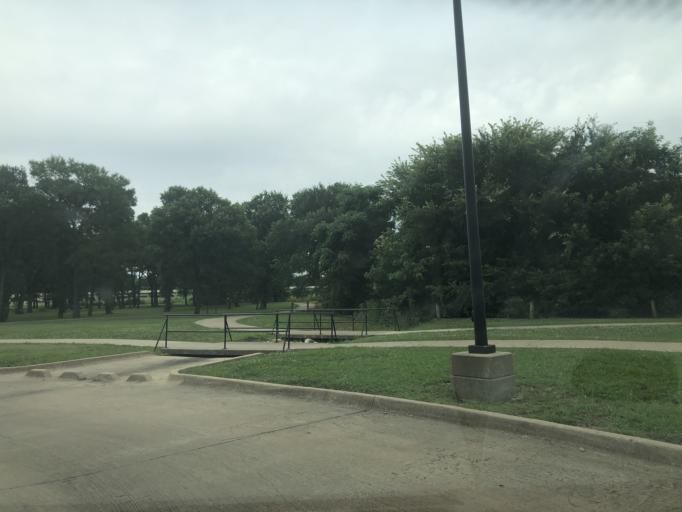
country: US
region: Texas
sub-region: Dallas County
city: Irving
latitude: 32.7847
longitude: -96.9776
